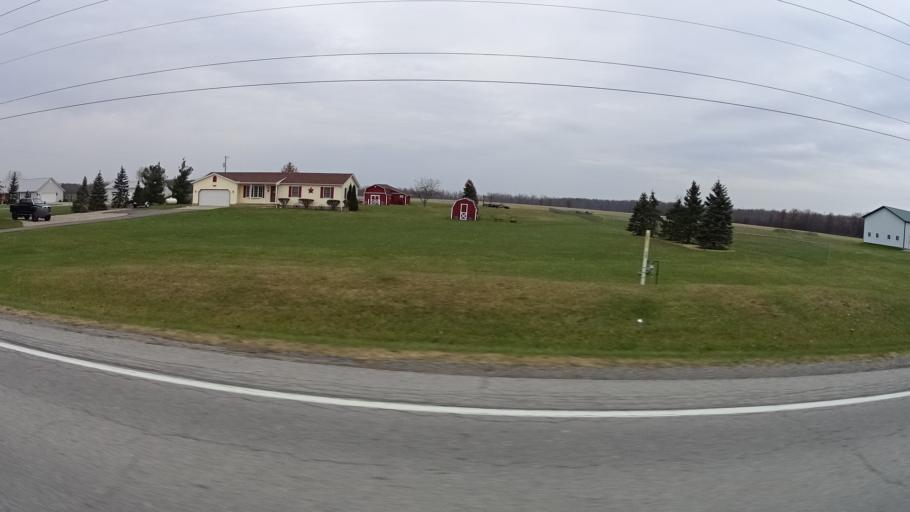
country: US
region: Ohio
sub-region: Lorain County
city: Wellington
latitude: 41.1687
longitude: -82.1574
